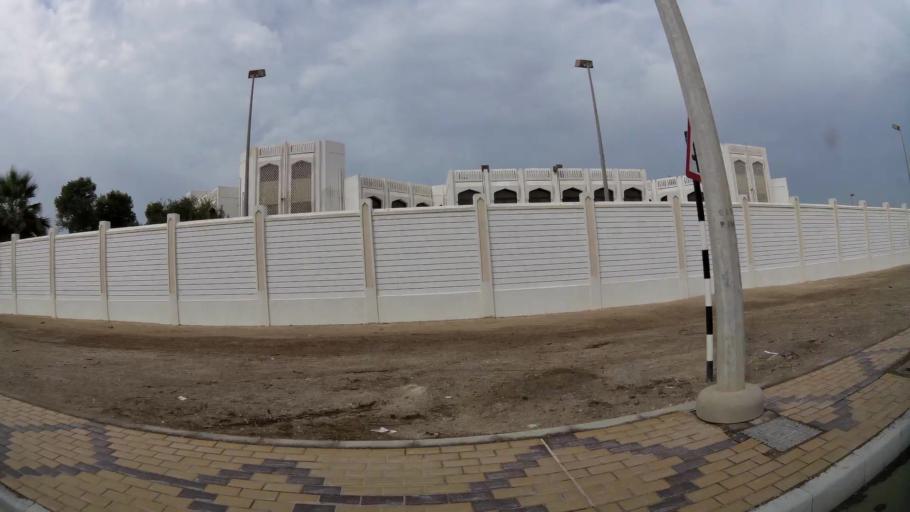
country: AE
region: Abu Dhabi
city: Abu Dhabi
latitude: 24.4418
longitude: 54.4368
